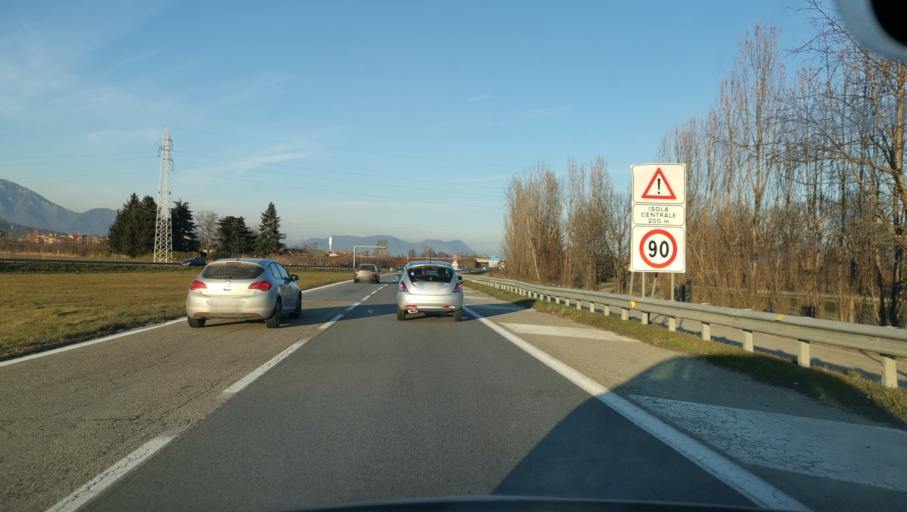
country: IT
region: Piedmont
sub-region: Provincia di Torino
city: Pinerolo
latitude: 44.8721
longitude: 7.3491
